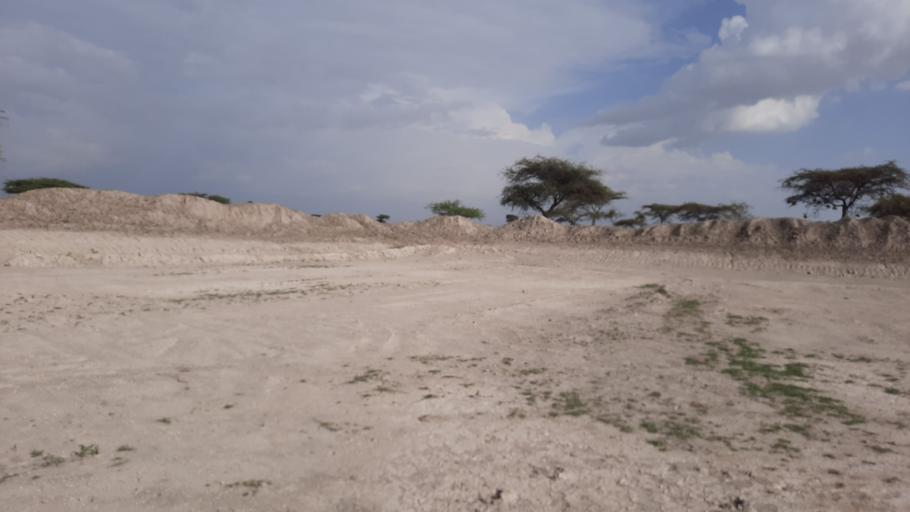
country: ET
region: Oromiya
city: Ziway
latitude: 7.6910
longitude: 38.6651
